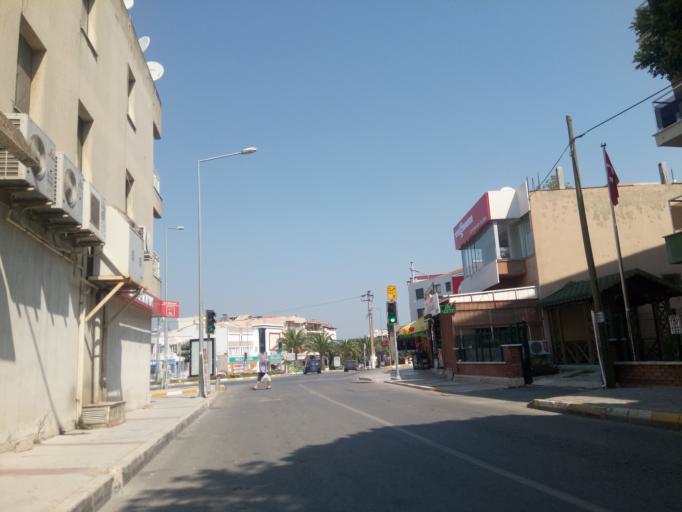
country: TR
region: Izmir
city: Urla
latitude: 38.3274
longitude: 26.7668
